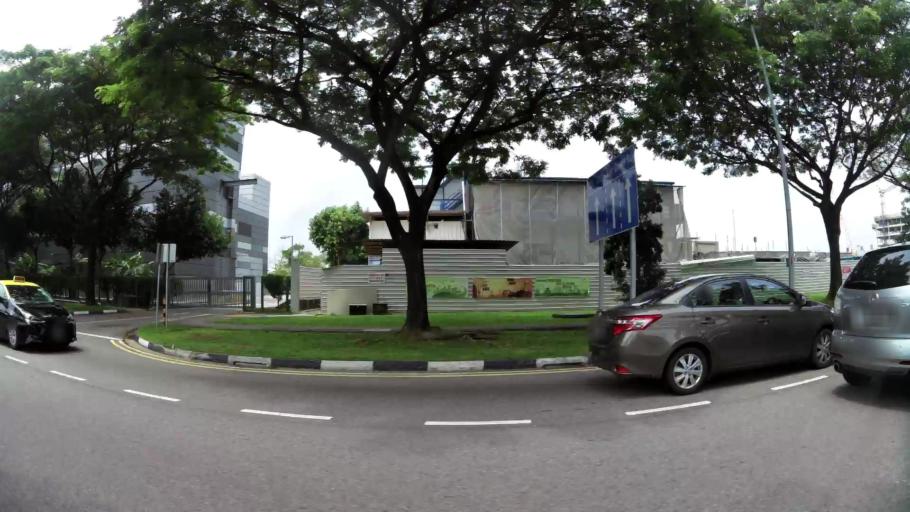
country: SG
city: Singapore
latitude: 1.3421
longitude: 103.8987
